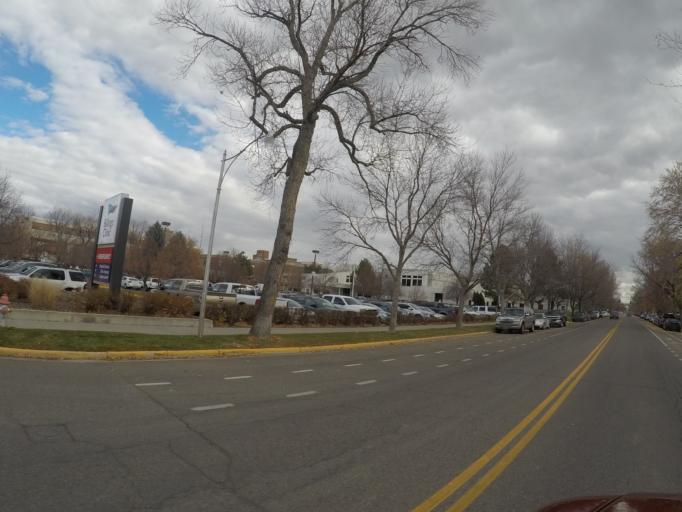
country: US
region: Montana
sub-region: Yellowstone County
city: Billings
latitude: 45.7892
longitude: -108.5164
